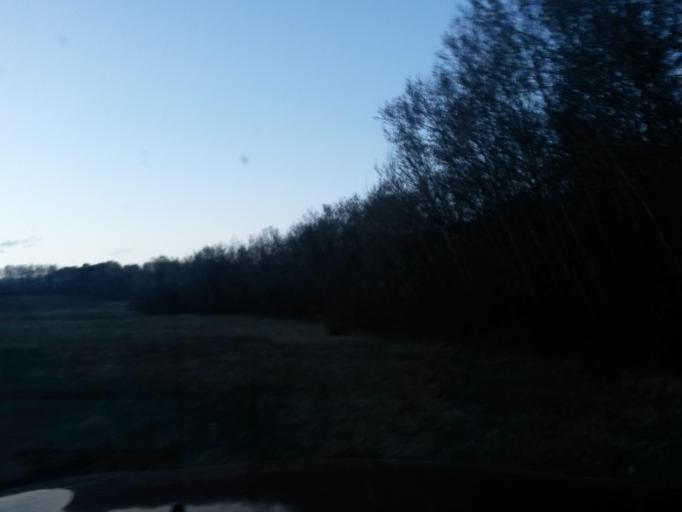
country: SK
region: Kosicky
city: Kosice
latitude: 48.7031
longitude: 21.3117
